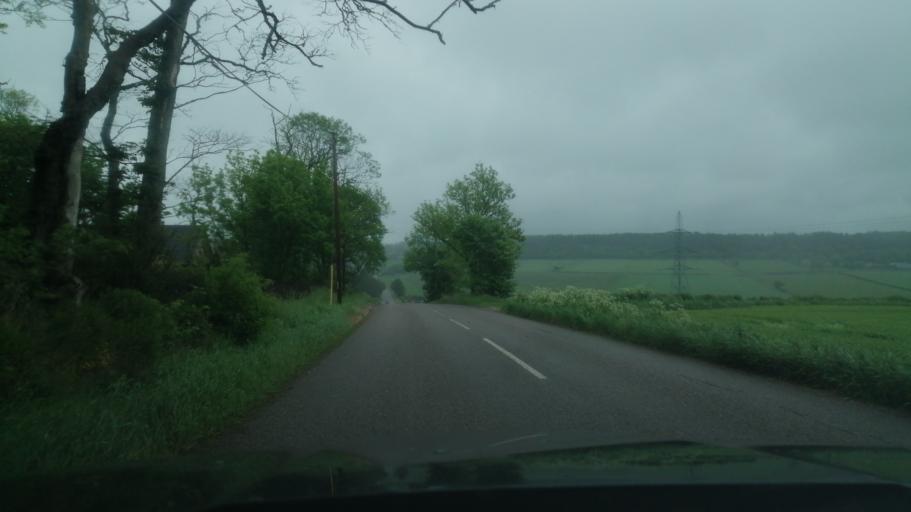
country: GB
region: Scotland
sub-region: Aberdeenshire
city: Huntly
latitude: 57.5465
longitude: -2.8152
